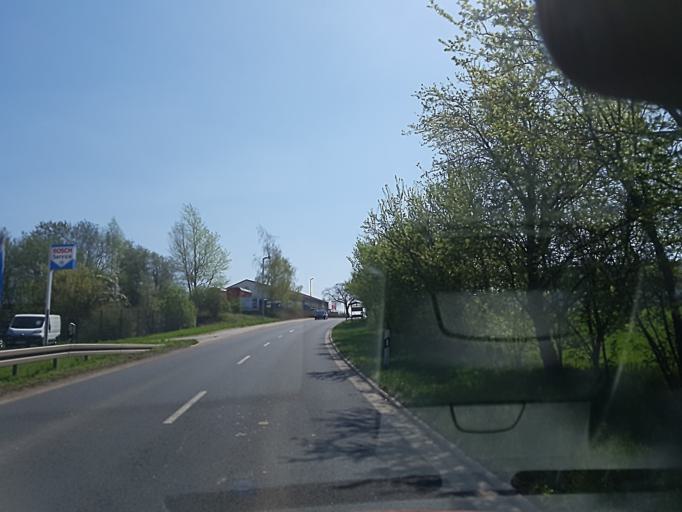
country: DE
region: Saxony
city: Leisnig
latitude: 51.1599
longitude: 12.9139
